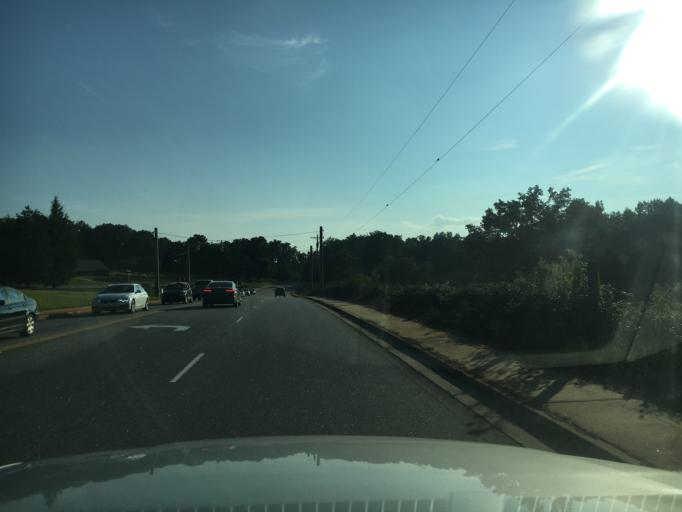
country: US
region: South Carolina
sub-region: Greenville County
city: Taylors
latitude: 34.8933
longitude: -82.2663
